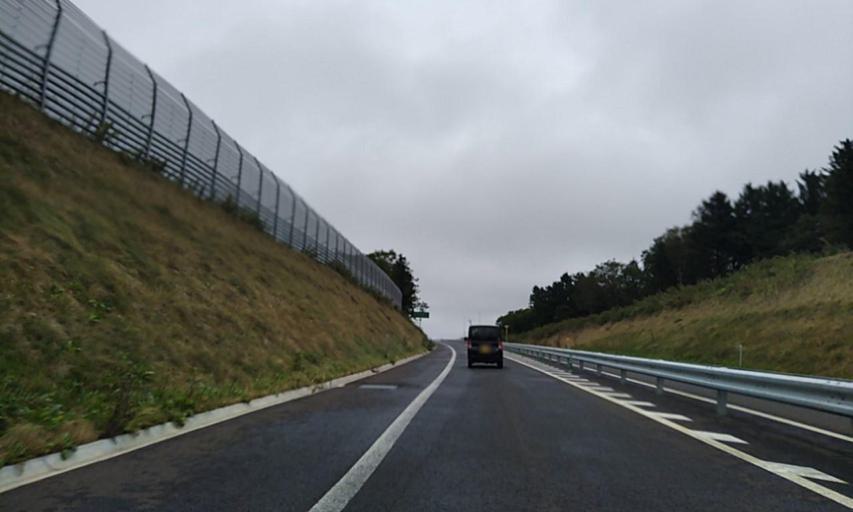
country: JP
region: Hokkaido
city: Nemuro
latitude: 43.2792
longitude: 145.5107
